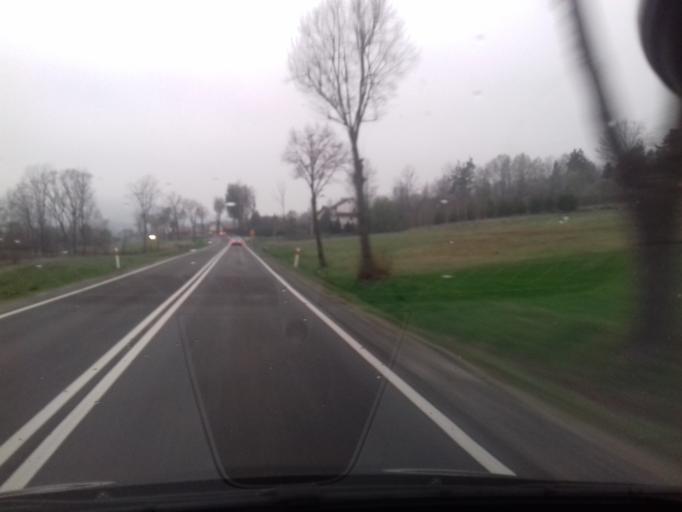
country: PL
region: Lesser Poland Voivodeship
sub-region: Powiat limanowski
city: Tymbark
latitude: 49.7224
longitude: 20.3593
